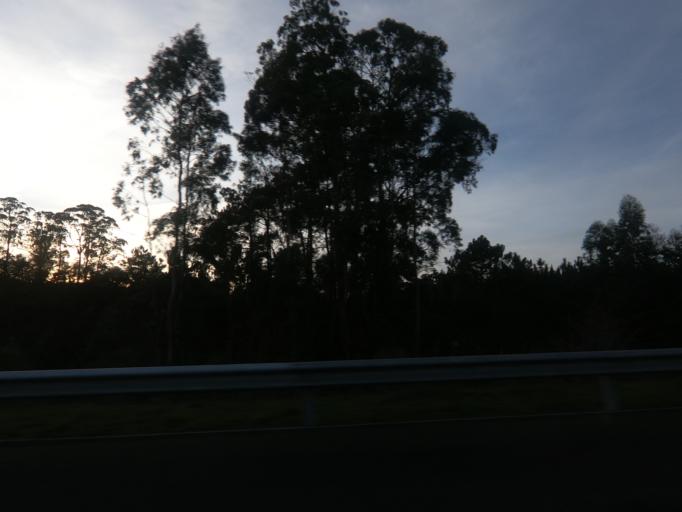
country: PT
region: Leiria
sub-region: Leiria
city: Santa Catarina da Serra
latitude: 39.6504
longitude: -8.6961
